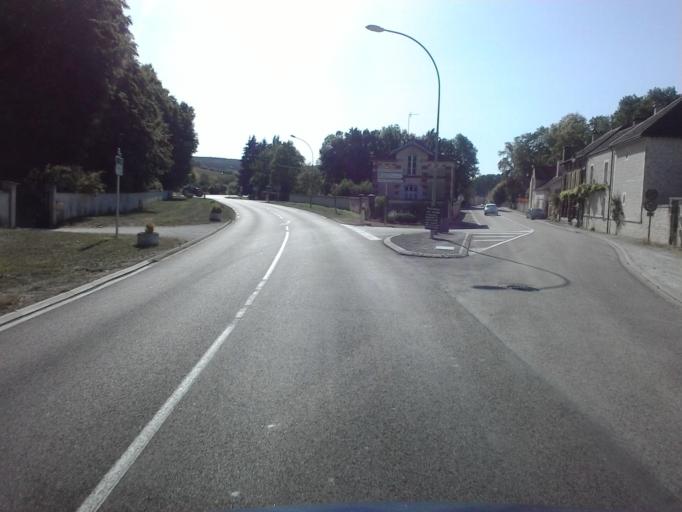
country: FR
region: Champagne-Ardenne
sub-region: Departement de l'Aube
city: Mussy-sur-Seine
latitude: 47.9818
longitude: 4.4972
